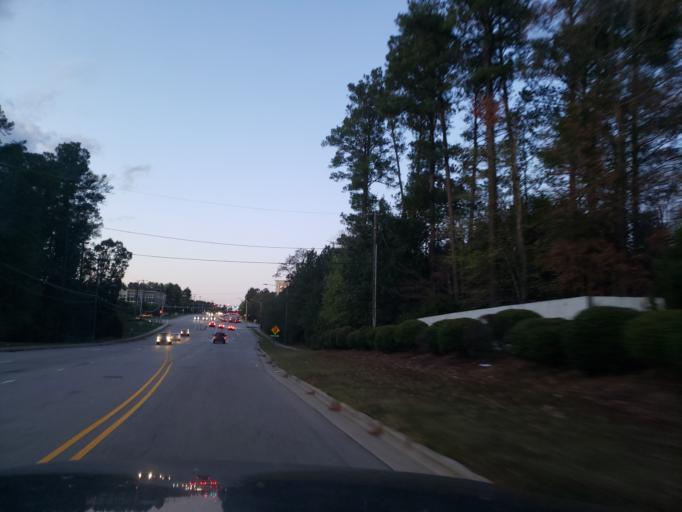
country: US
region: North Carolina
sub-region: Orange County
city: Chapel Hill
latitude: 35.8991
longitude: -78.9592
